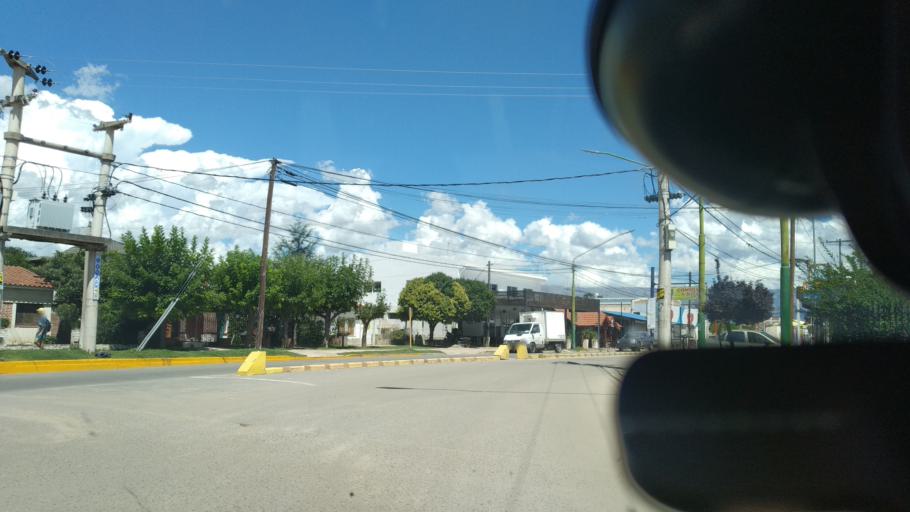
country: AR
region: Cordoba
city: Villa Cura Brochero
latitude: -31.7092
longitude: -65.0167
